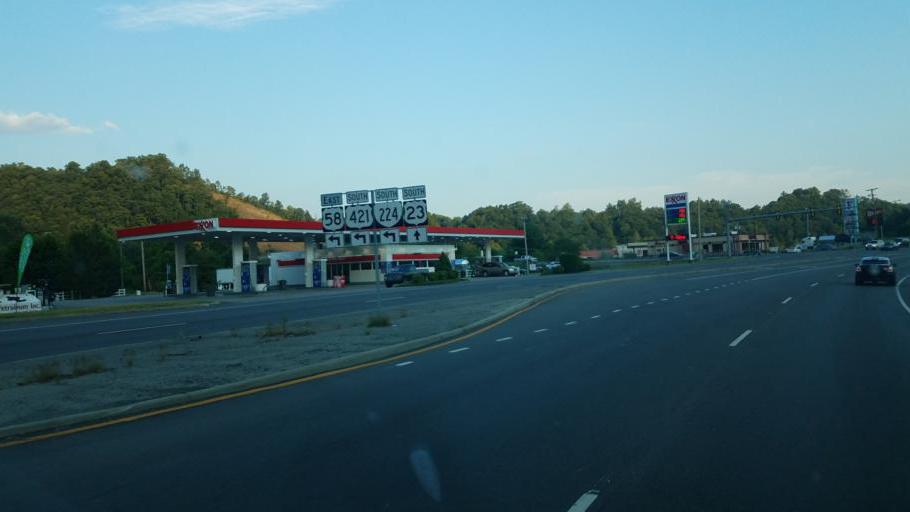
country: US
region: Virginia
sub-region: Scott County
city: Weber City
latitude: 36.6322
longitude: -82.5526
